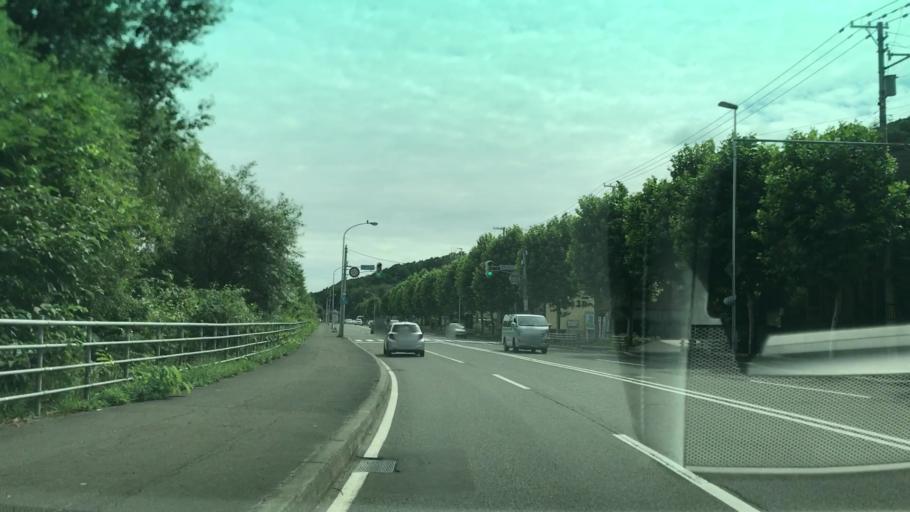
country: JP
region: Hokkaido
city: Sapporo
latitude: 42.9861
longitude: 141.3483
